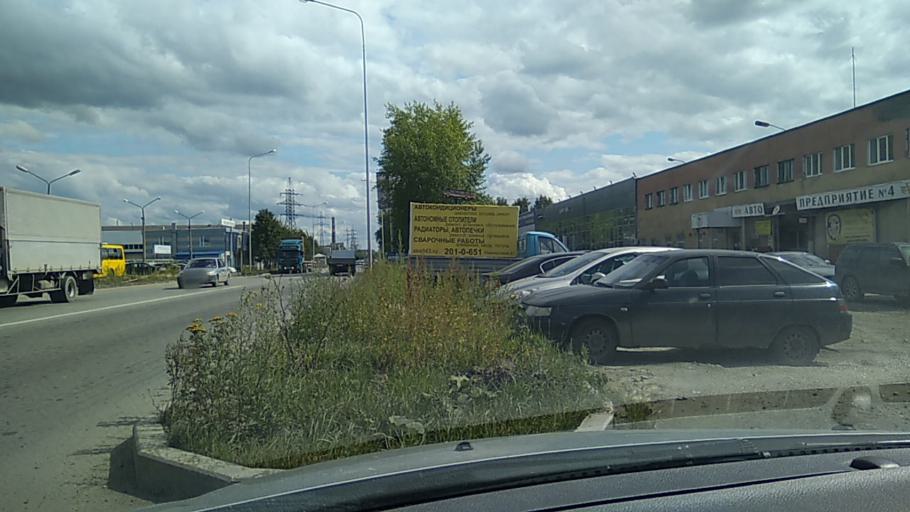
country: RU
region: Sverdlovsk
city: Shuvakish
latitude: 56.8864
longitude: 60.5292
